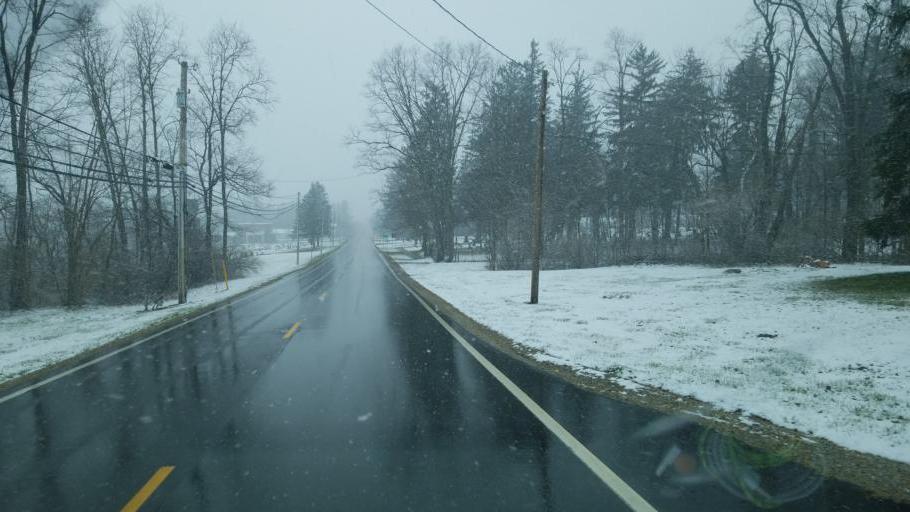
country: US
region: Ohio
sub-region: Preble County
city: New Paris
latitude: 39.8477
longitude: -84.7926
